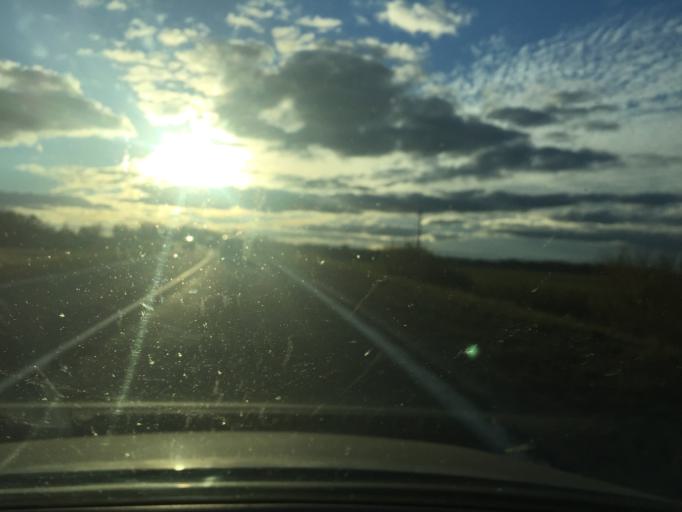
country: BY
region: Vitebsk
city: Vyerkhnyadzvinsk
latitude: 55.8356
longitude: 27.8280
